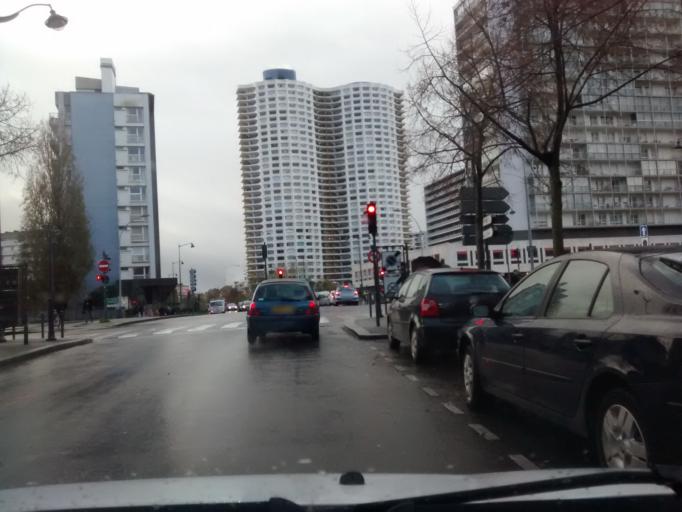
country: FR
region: Brittany
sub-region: Departement d'Ille-et-Vilaine
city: Rennes
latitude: 48.1124
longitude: -1.6863
